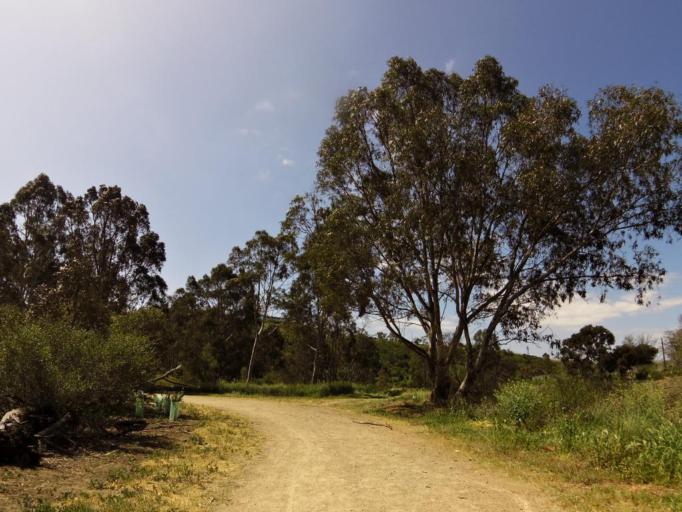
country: AU
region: Victoria
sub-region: Moonee Valley
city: Essendon West
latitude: -37.7577
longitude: 144.8798
